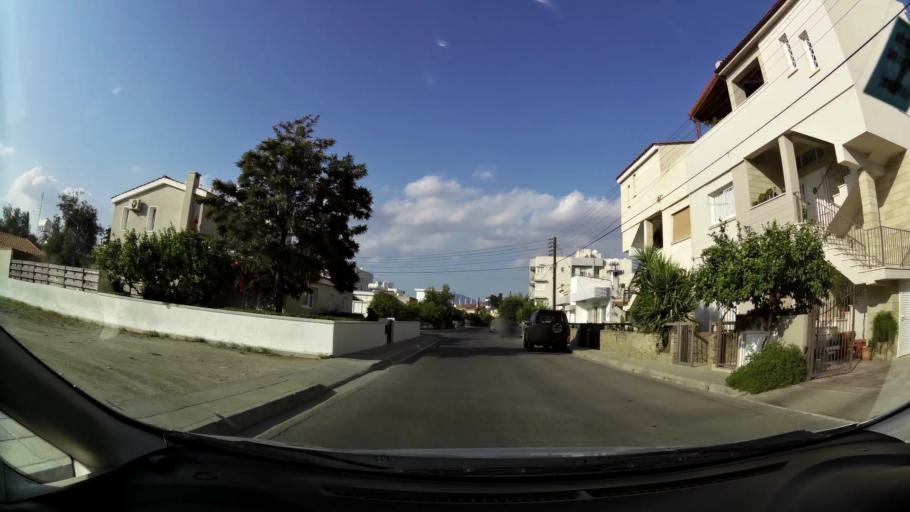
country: CY
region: Lefkosia
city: Nicosia
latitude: 35.1725
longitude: 33.3270
